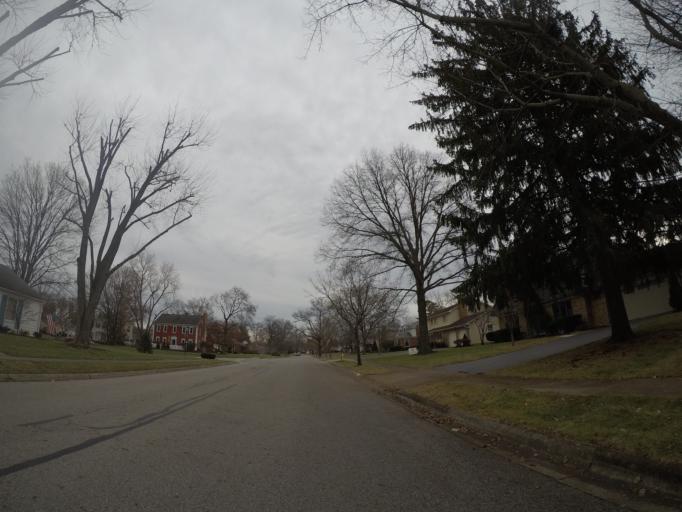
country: US
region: Ohio
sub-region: Franklin County
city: Upper Arlington
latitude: 40.0303
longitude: -83.0700
